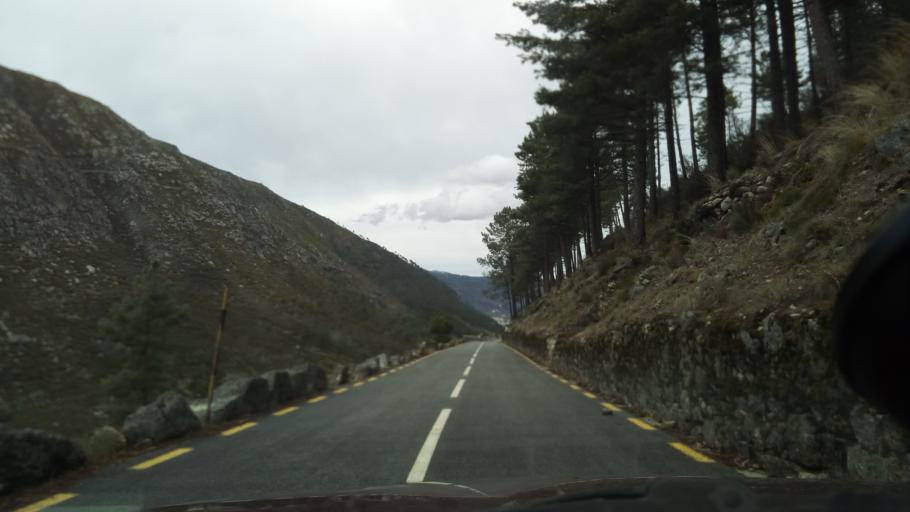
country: PT
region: Guarda
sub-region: Manteigas
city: Manteigas
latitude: 40.3515
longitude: -7.5596
